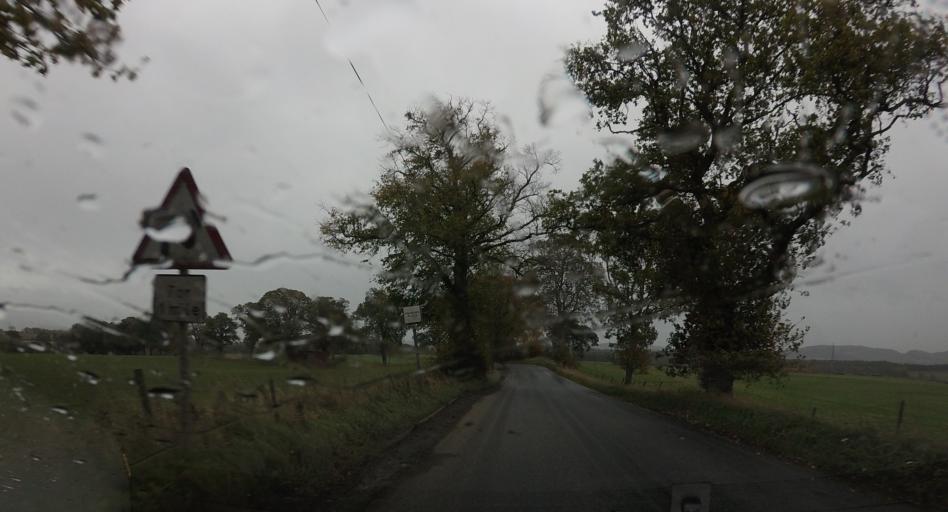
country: GB
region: Scotland
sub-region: Perth and Kinross
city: Blairgowrie
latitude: 56.5422
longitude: -3.3389
